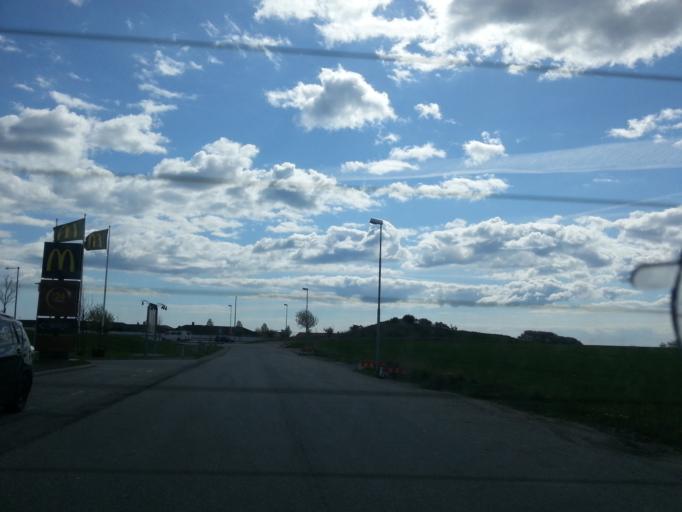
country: SE
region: Skane
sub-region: Ystads Kommun
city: Ystad
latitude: 55.4375
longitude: 13.7903
